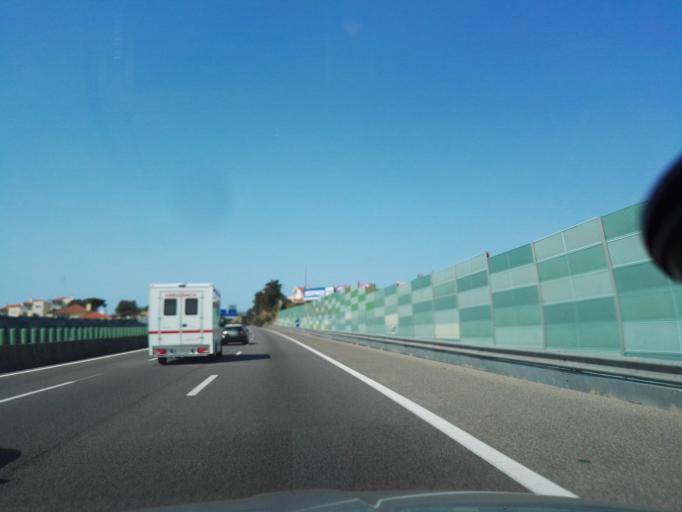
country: PT
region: Lisbon
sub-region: Cascais
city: Estoril
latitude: 38.7181
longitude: -9.3789
